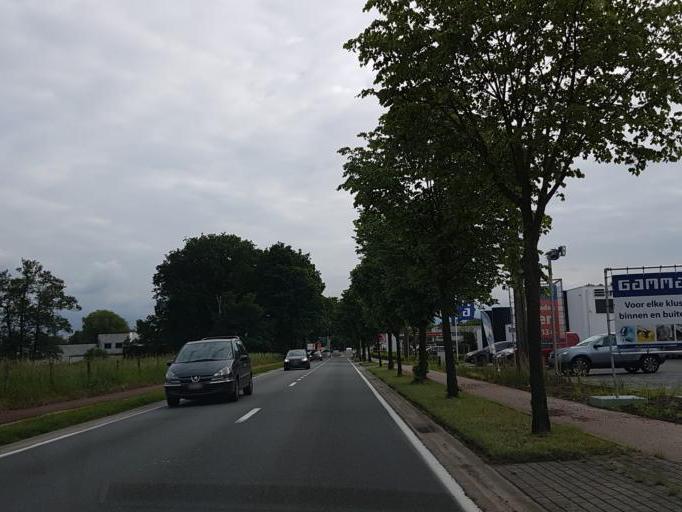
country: BE
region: Flanders
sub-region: Provincie Antwerpen
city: Zoersel
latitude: 51.2485
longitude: 4.7052
